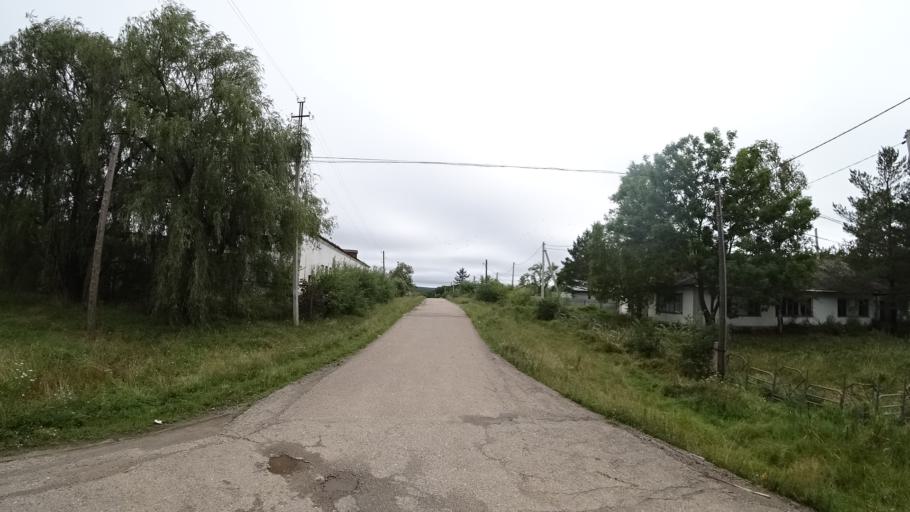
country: RU
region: Primorskiy
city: Monastyrishche
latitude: 44.0814
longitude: 132.5830
